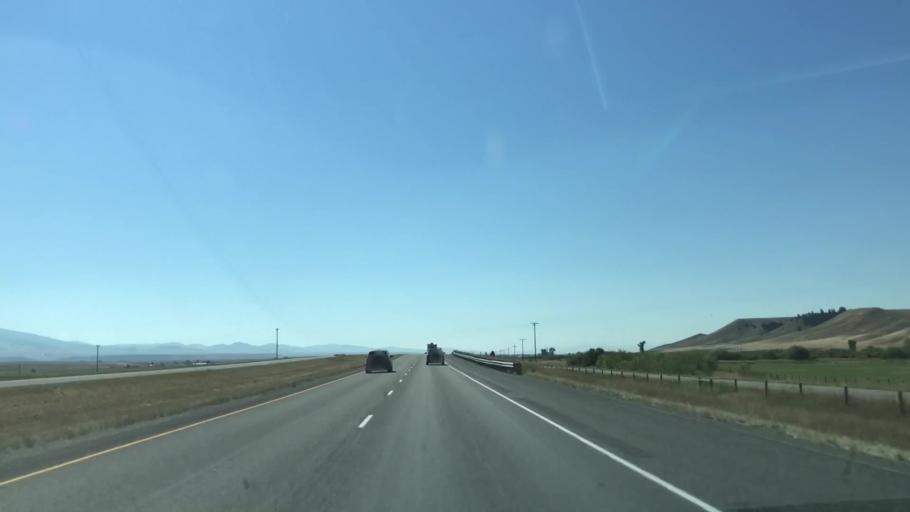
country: US
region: Montana
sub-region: Powell County
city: Deer Lodge
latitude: 46.4794
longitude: -112.7237
